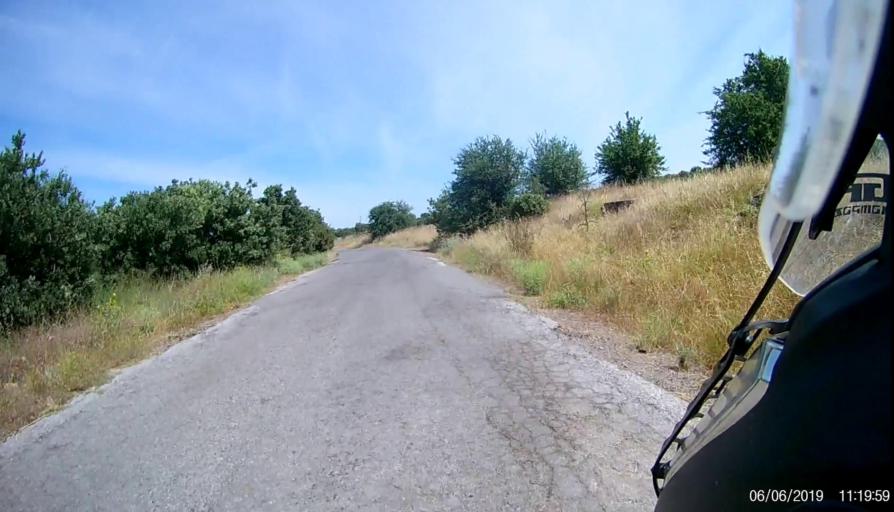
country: TR
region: Canakkale
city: Gulpinar
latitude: 39.6620
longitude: 26.1639
